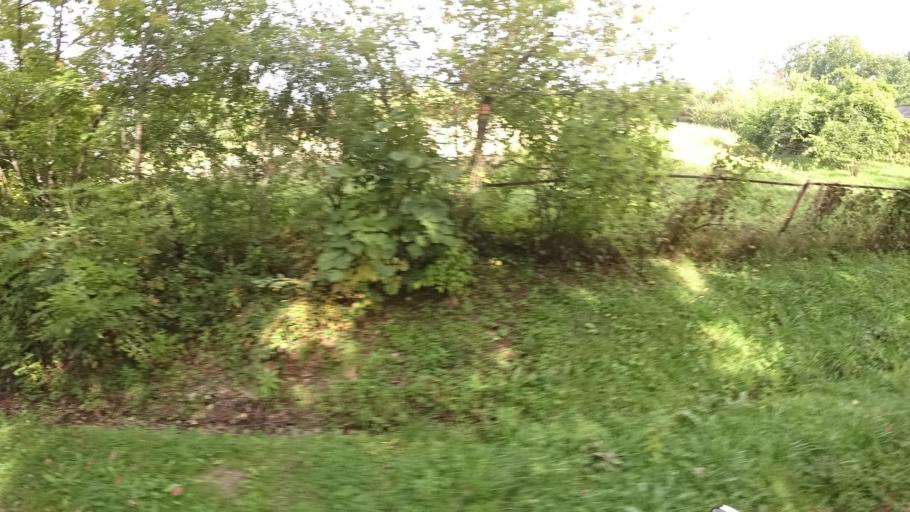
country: RU
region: Primorskiy
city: Dostoyevka
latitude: 44.3234
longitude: 133.4851
